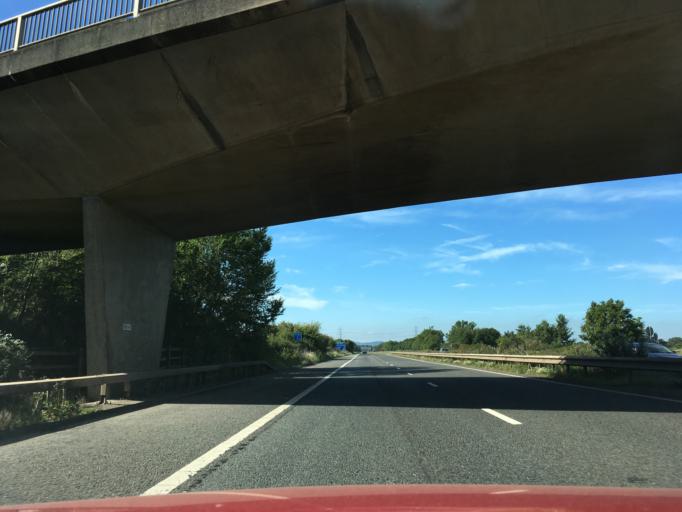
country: GB
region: England
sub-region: South Gloucestershire
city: Almondsbury
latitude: 51.5760
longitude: -2.5868
